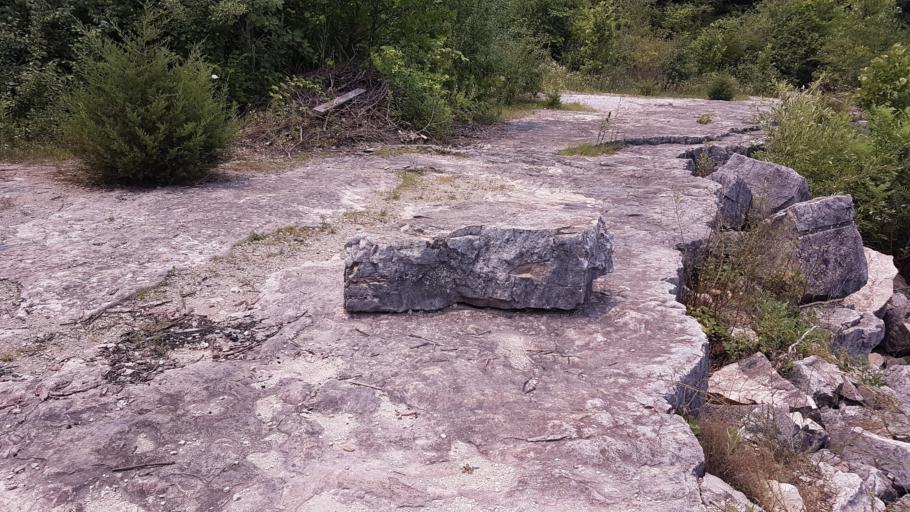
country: US
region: Ohio
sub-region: Wood County
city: Perrysburg
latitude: 41.5431
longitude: -83.5656
